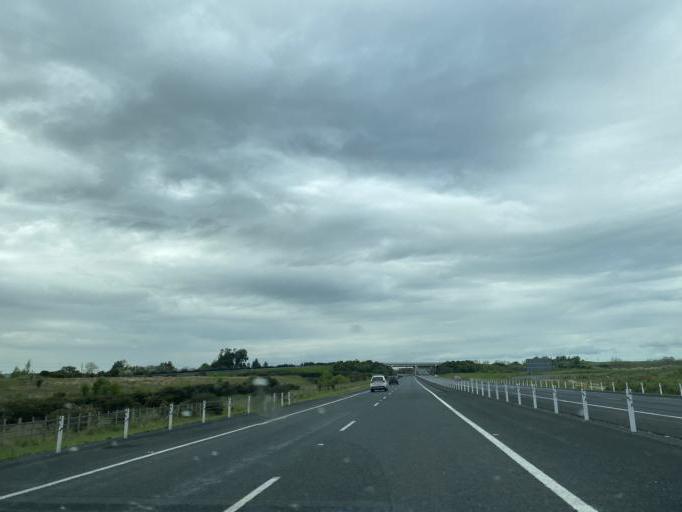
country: NZ
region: Waikato
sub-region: Waikato District
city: Ngaruawahia
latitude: -37.6907
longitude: 175.2142
